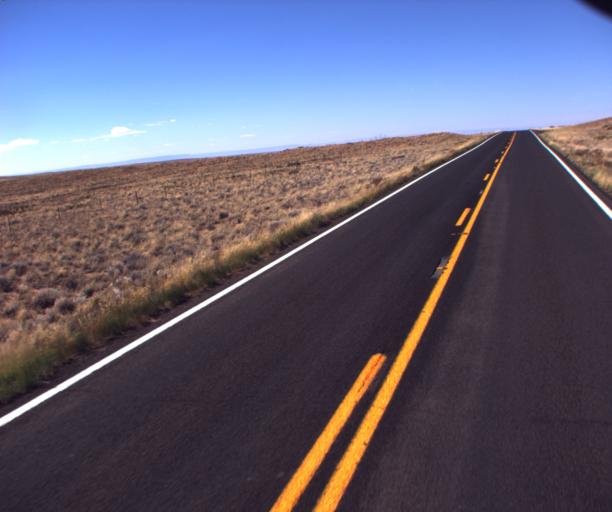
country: US
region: Arizona
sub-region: Coconino County
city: Tuba City
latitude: 35.9690
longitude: -110.9592
